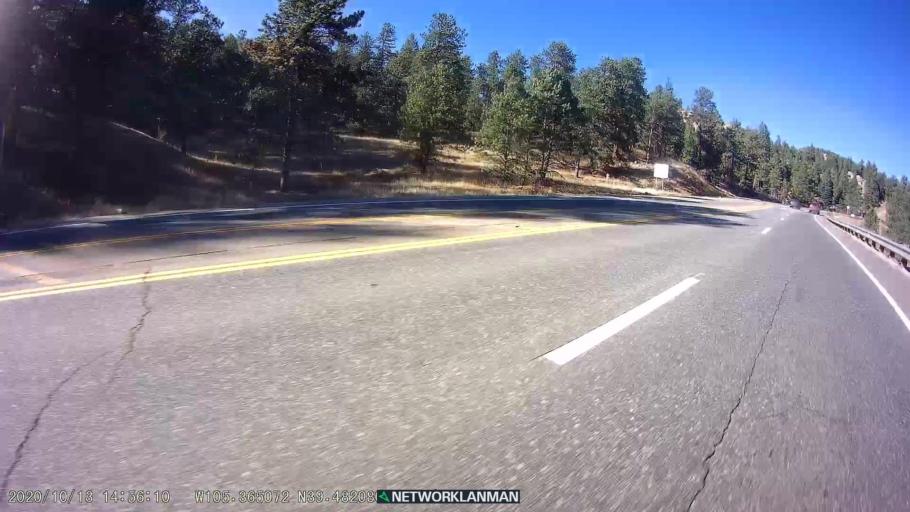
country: US
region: Colorado
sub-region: Jefferson County
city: Evergreen
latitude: 39.4823
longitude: -105.3650
